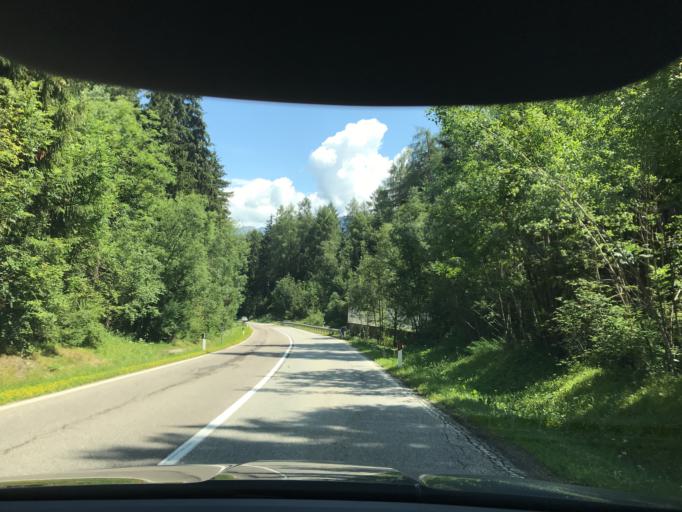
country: IT
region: Trentino-Alto Adige
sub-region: Bolzano
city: Valdaora di Mezzo
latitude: 46.7525
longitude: 12.0176
